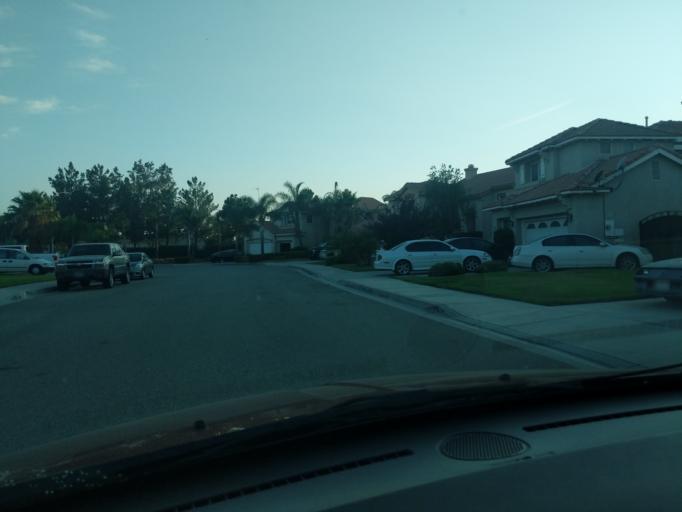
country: US
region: California
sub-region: San Bernardino County
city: Muscoy
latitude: 34.1542
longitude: -117.3942
